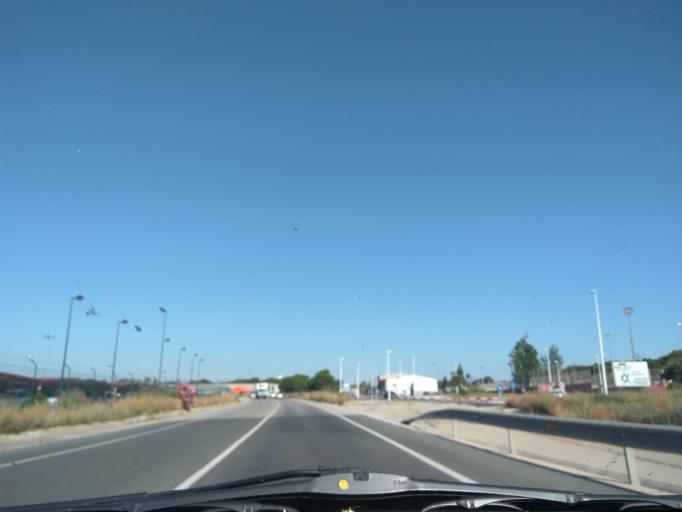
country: ES
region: Valencia
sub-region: Provincia de Valencia
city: Manises
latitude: 39.4955
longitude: -0.4759
